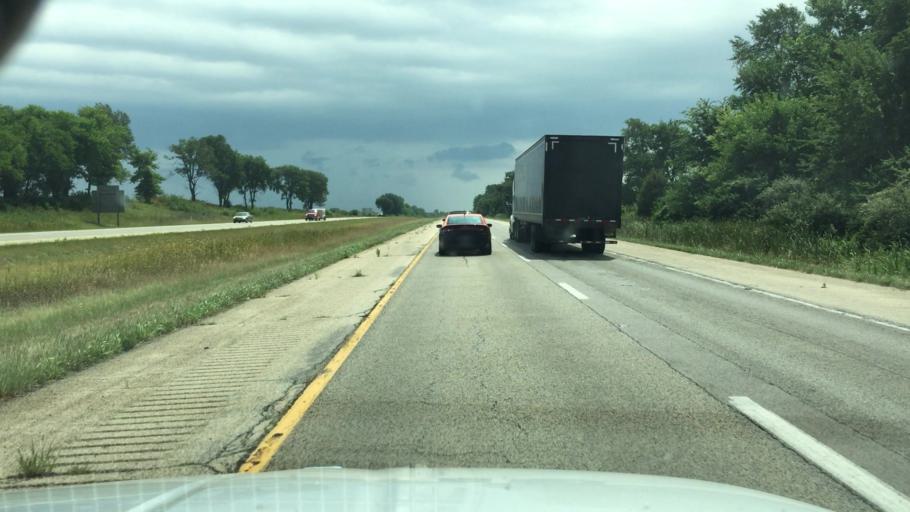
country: US
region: Illinois
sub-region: Peoria County
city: Elmwood
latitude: 40.8167
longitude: -89.8517
